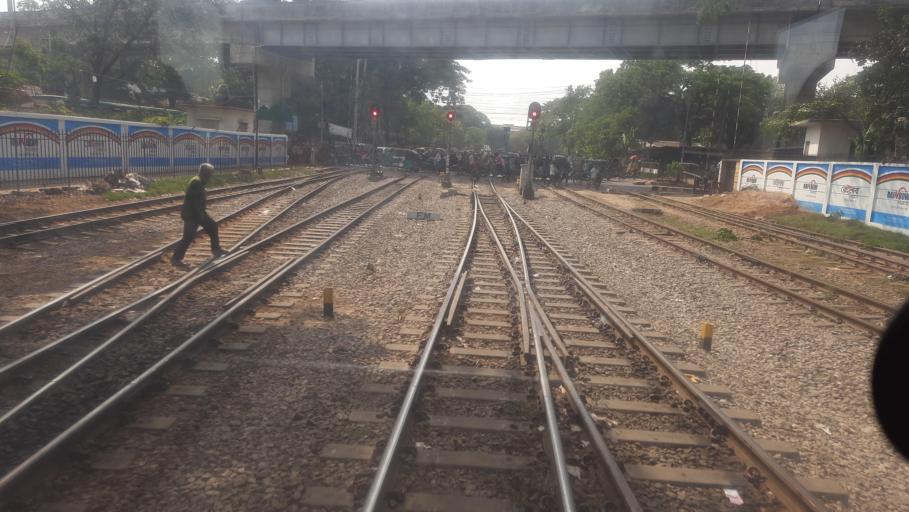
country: BD
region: Chittagong
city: Chittagong
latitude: 22.3359
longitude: 91.8217
